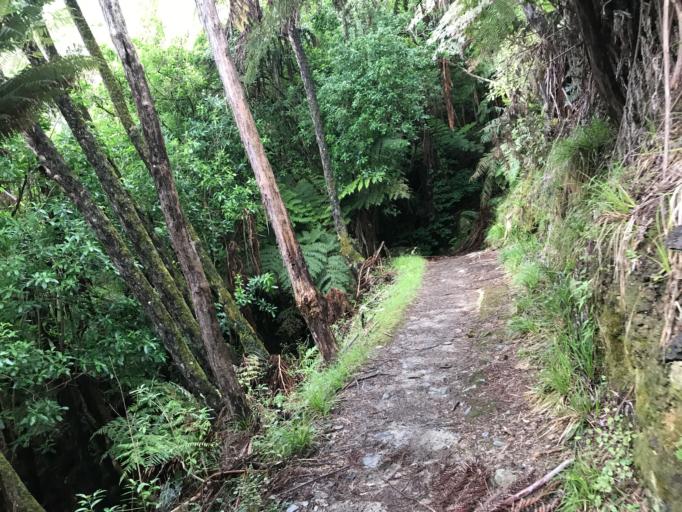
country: NZ
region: Marlborough
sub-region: Marlborough District
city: Picton
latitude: -41.2314
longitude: 173.9576
